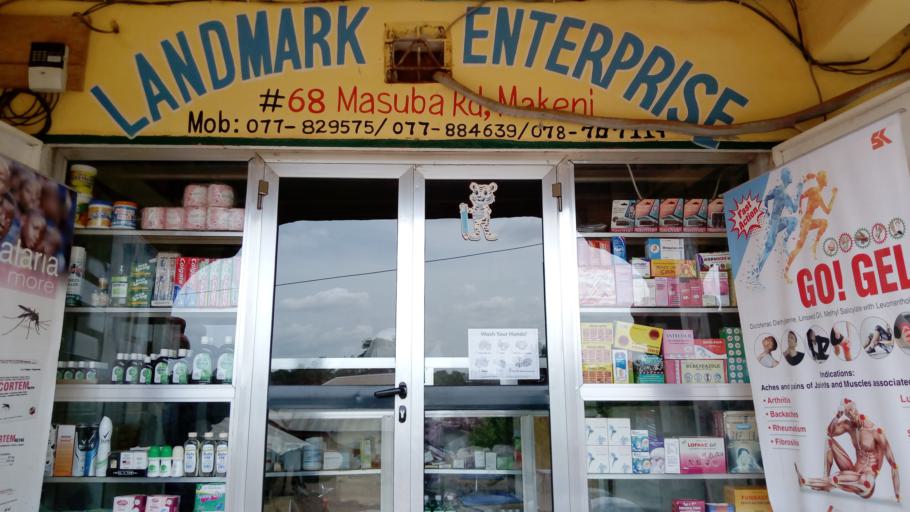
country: SL
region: Northern Province
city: Makeni
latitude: 8.8936
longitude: -12.0341
